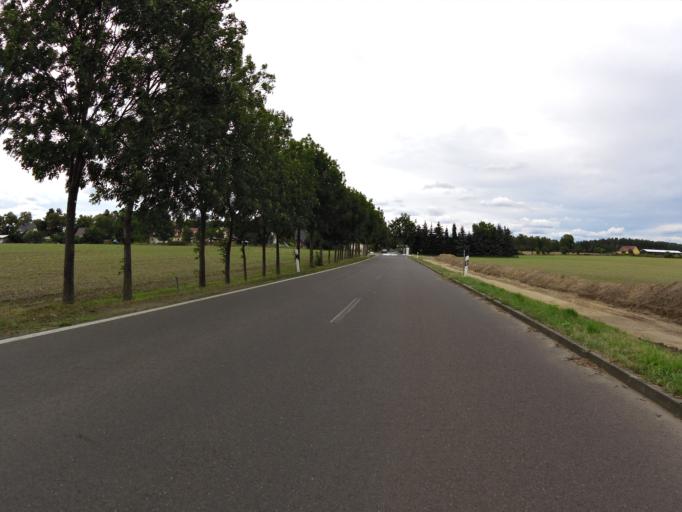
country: DE
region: Brandenburg
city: Reichenwalde
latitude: 52.2341
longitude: 13.9949
